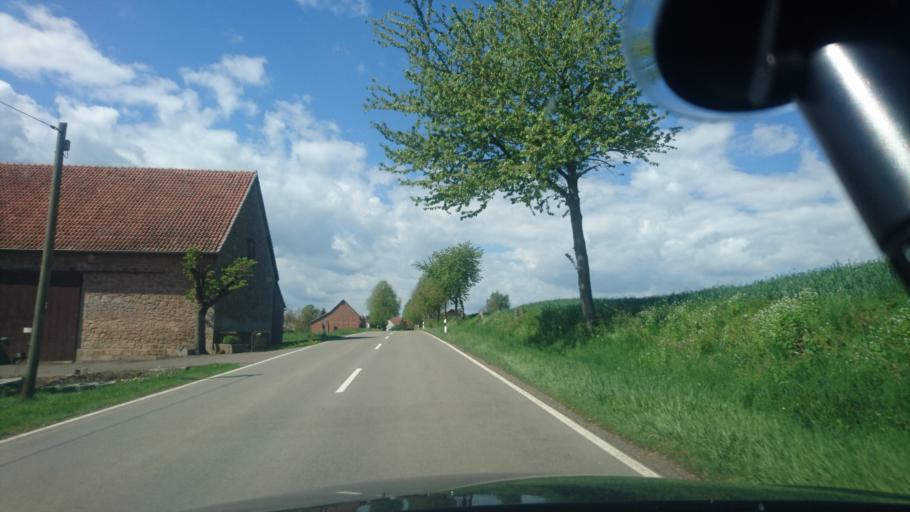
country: DE
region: North Rhine-Westphalia
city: Marsberg
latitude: 51.3863
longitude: 8.9002
